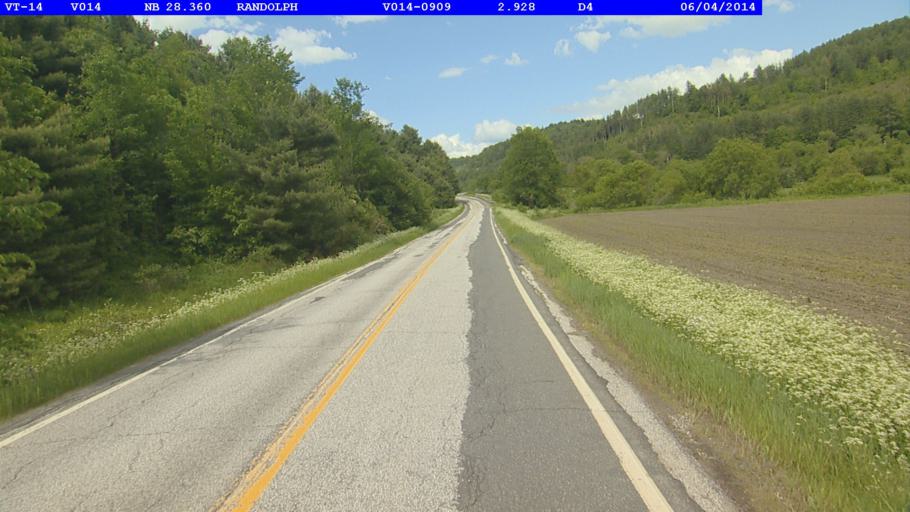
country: US
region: Vermont
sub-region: Orange County
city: Randolph
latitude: 43.9124
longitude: -72.5591
